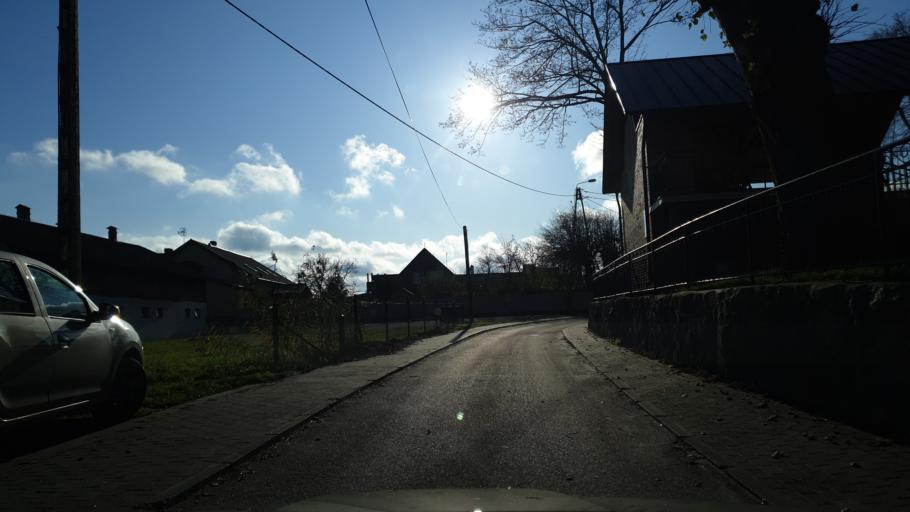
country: PL
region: Pomeranian Voivodeship
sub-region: Powiat pucki
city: Gniezdzewo
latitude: 54.7602
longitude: 18.4006
